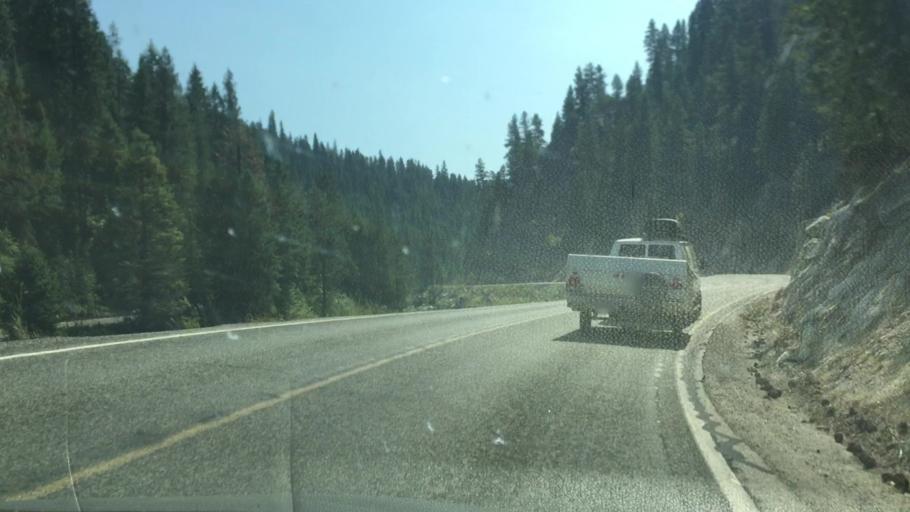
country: US
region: Idaho
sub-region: Valley County
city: Cascade
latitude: 44.3168
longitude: -116.0680
